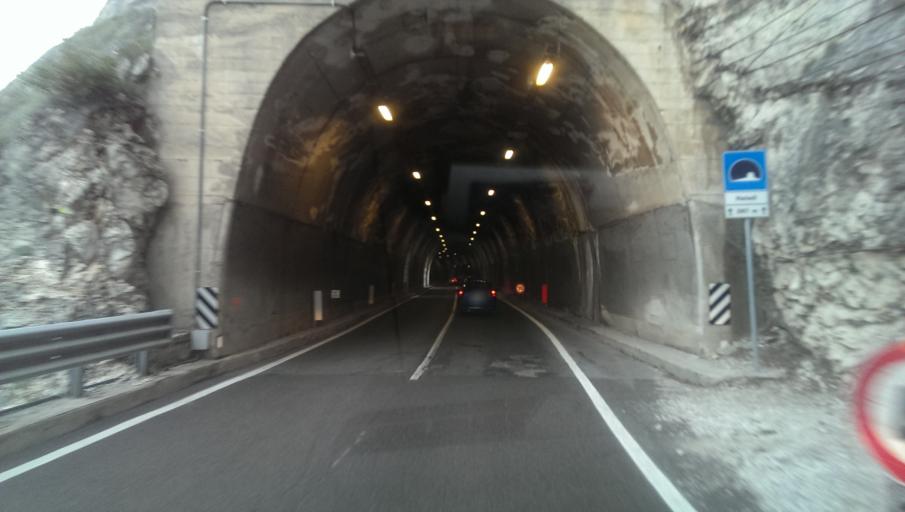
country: IT
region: Lombardy
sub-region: Provincia di Brescia
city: Limone sul Garda
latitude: 45.8376
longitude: 10.8255
